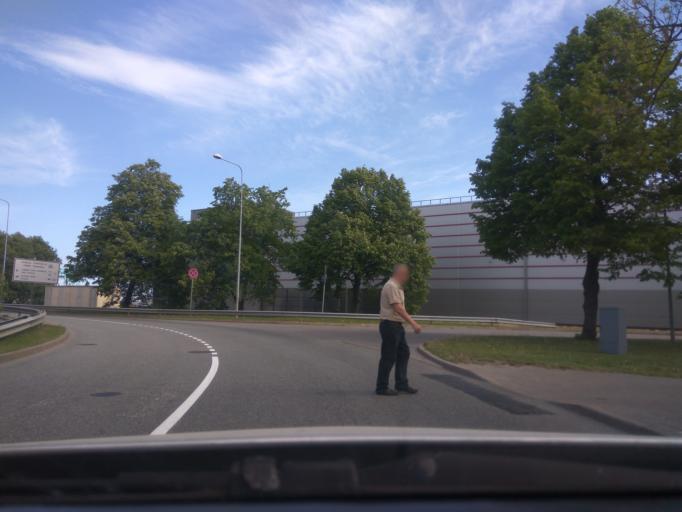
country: LV
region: Ventspils
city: Ventspils
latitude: 57.3895
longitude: 21.5835
